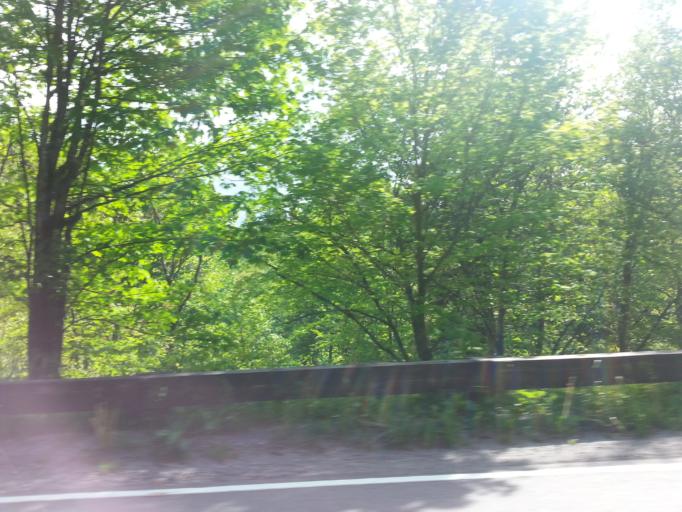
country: US
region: Tennessee
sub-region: Sevier County
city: Gatlinburg
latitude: 35.6127
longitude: -83.4233
